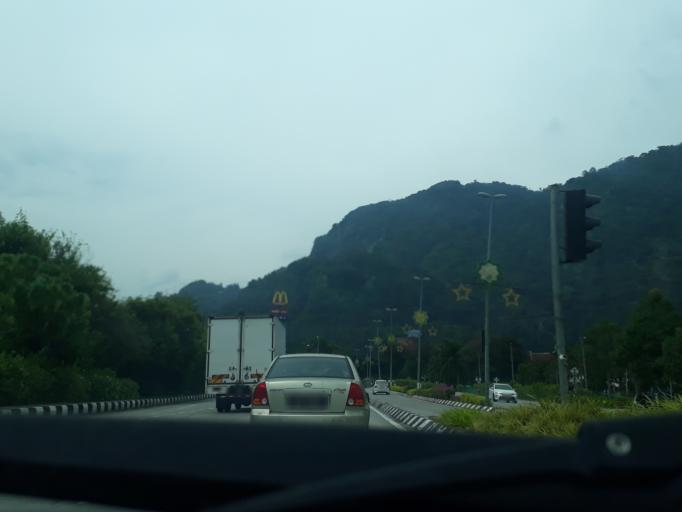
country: MY
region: Perak
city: Ipoh
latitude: 4.6234
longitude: 101.1504
